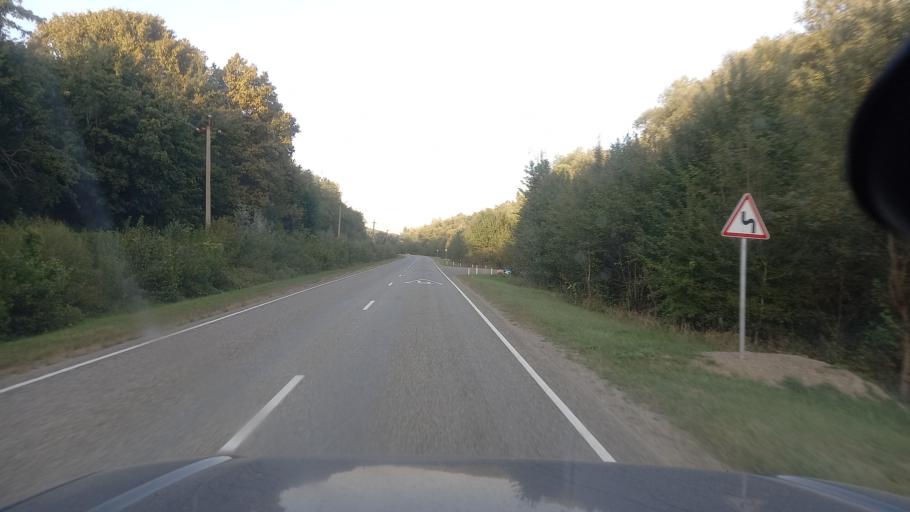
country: RU
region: Krasnodarskiy
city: Smolenskaya
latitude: 44.7352
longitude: 38.7230
